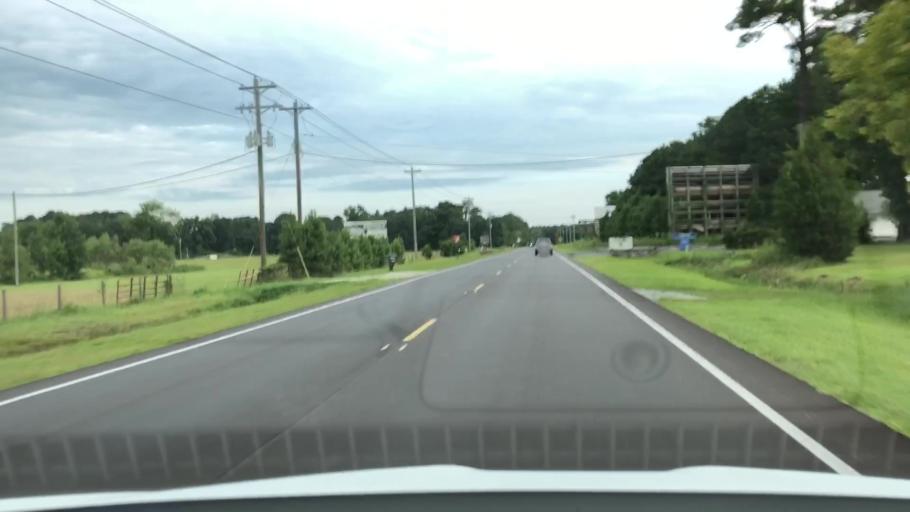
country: US
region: North Carolina
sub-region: Jones County
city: Maysville
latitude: 34.8640
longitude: -77.1908
